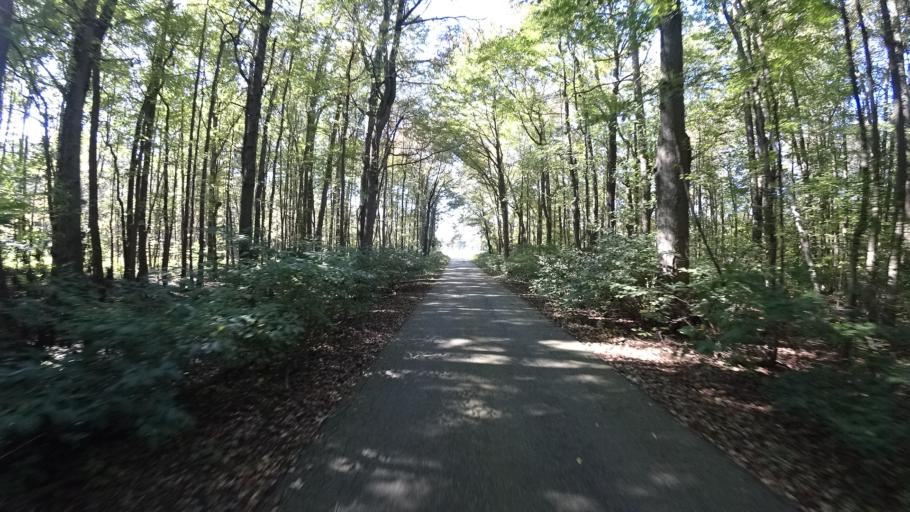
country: US
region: Indiana
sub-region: LaPorte County
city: Long Beach
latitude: 41.7455
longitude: -86.8237
